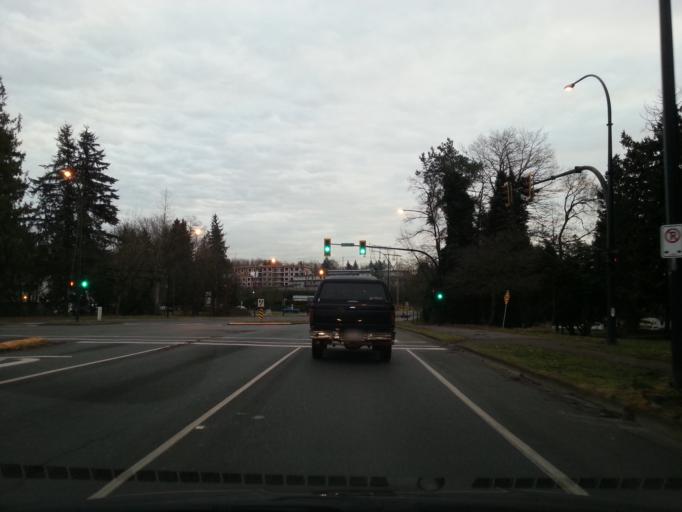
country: CA
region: British Columbia
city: New Westminster
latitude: 49.1806
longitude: -122.8419
